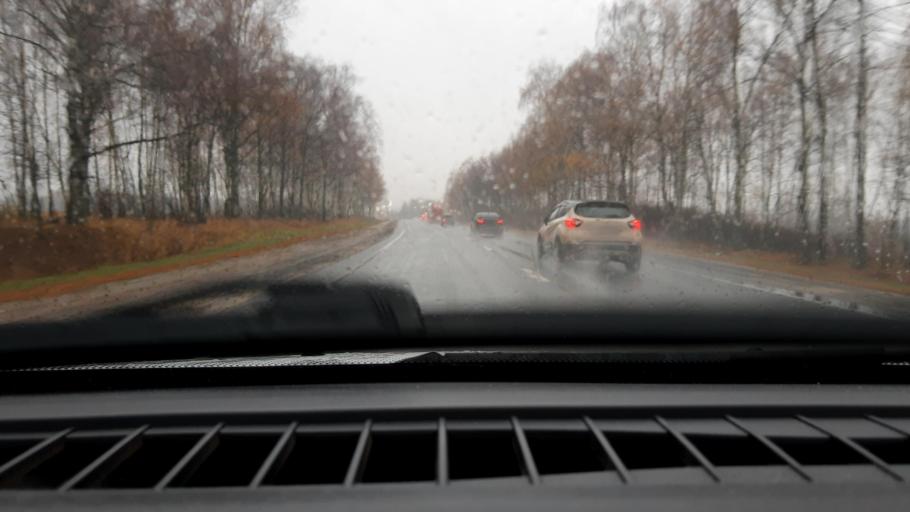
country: RU
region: Nizjnij Novgorod
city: Sitniki
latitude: 56.5115
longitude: 44.0238
